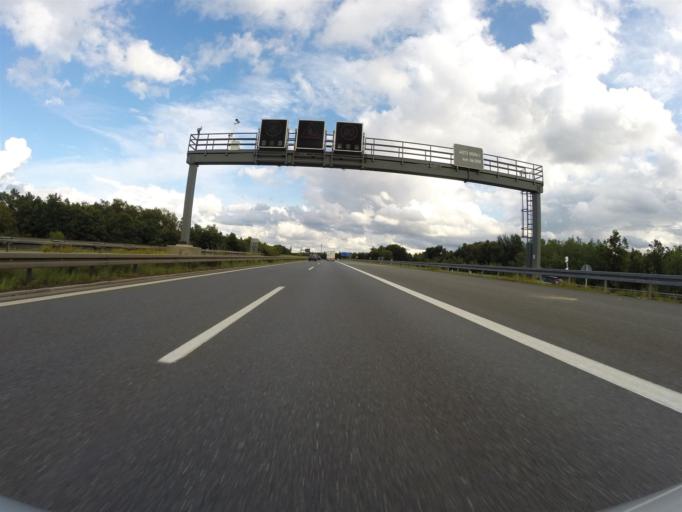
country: DE
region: Bavaria
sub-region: Regierungsbezirk Mittelfranken
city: Wendelstein
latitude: 49.3793
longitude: 11.1341
